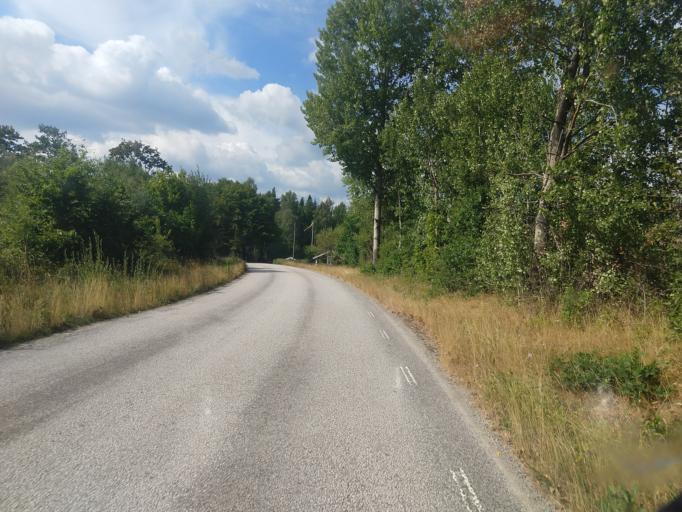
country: SE
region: Blekinge
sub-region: Karlskrona Kommun
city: Rodeby
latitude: 56.2377
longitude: 15.5735
